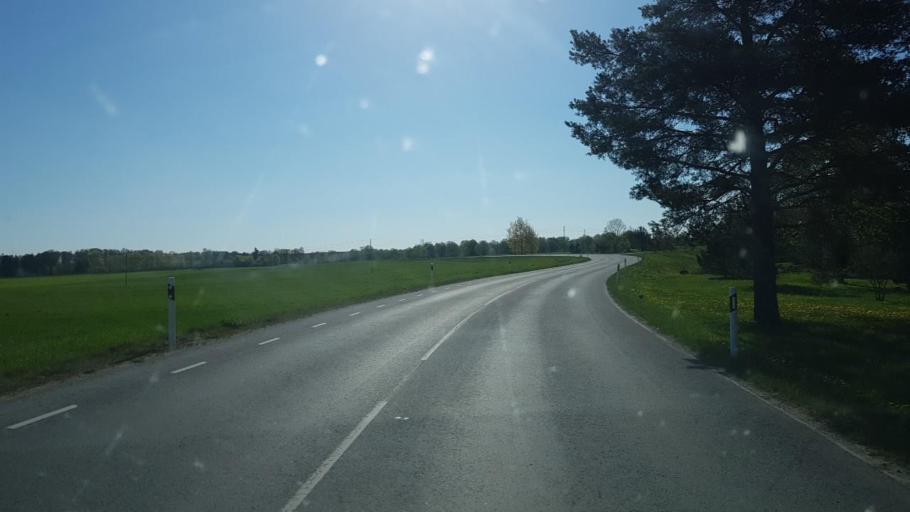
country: EE
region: Harju
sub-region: Kuusalu vald
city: Kuusalu
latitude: 59.4532
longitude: 25.4201
